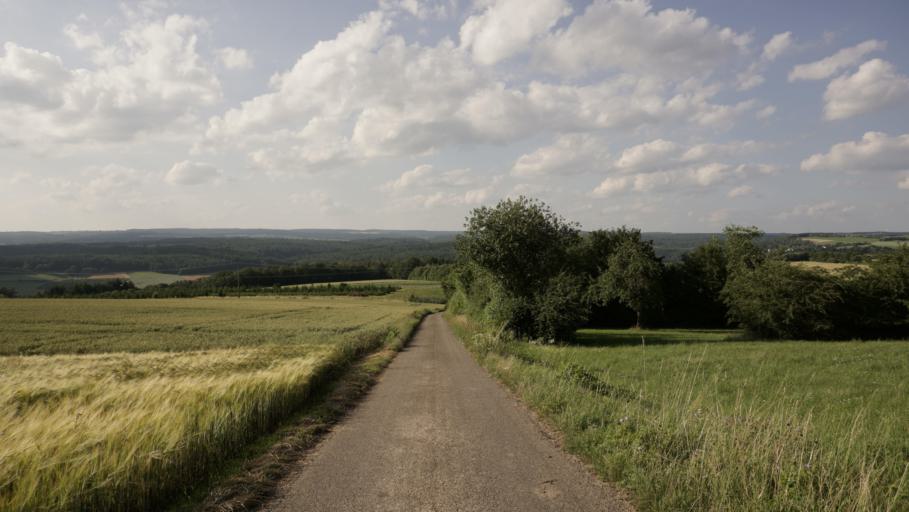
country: DE
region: Baden-Wuerttemberg
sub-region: Karlsruhe Region
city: Mosbach
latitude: 49.3709
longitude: 9.1851
